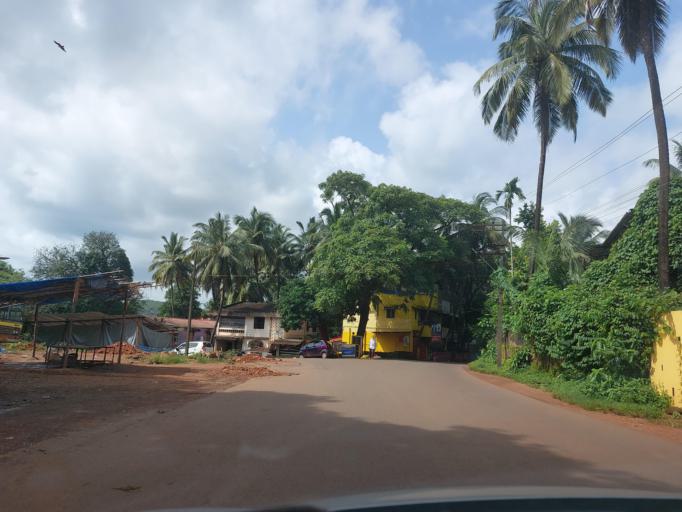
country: IN
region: Goa
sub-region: North Goa
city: Ponda
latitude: 15.3994
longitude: 74.0084
